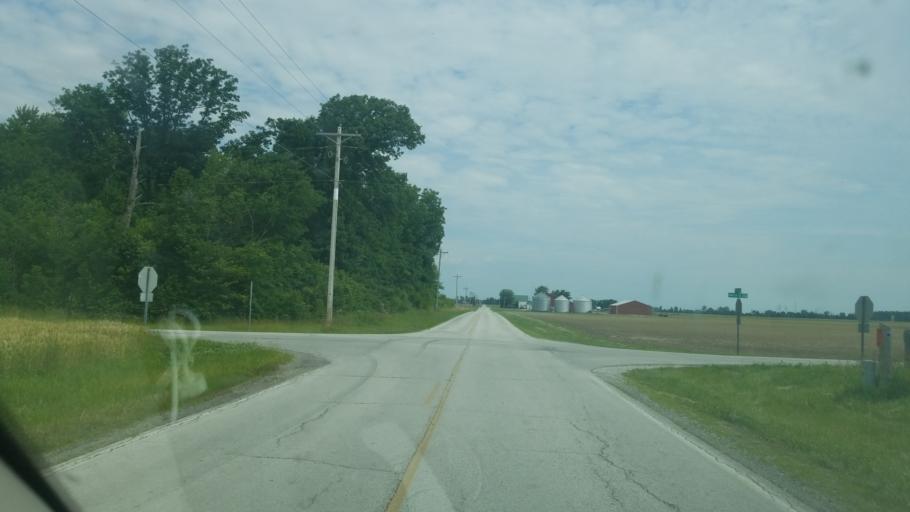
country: US
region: Ohio
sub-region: Seneca County
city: Fostoria
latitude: 41.1078
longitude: -83.4786
